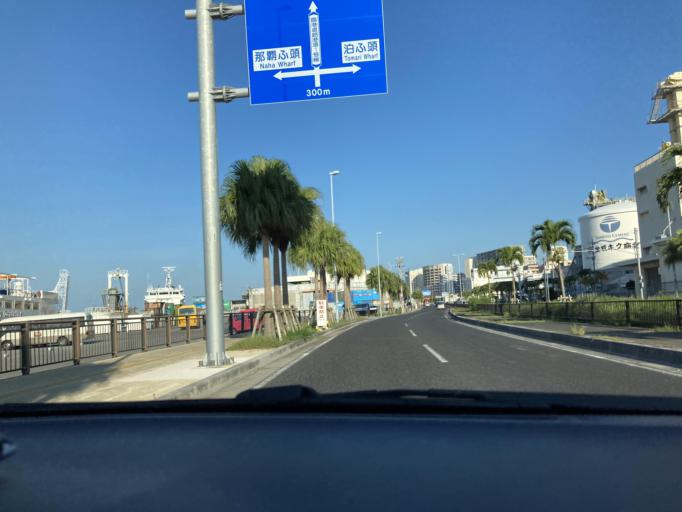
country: JP
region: Okinawa
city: Naha-shi
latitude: 26.2098
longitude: 127.6727
